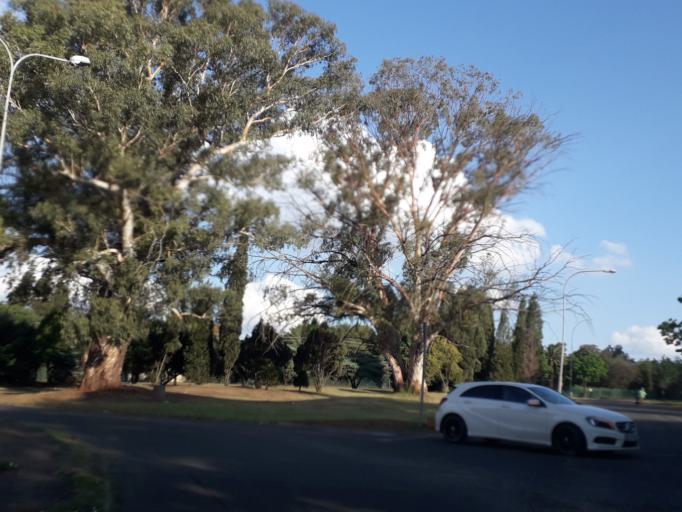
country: ZA
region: Gauteng
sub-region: City of Johannesburg Metropolitan Municipality
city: Johannesburg
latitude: -26.1523
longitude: 27.9973
